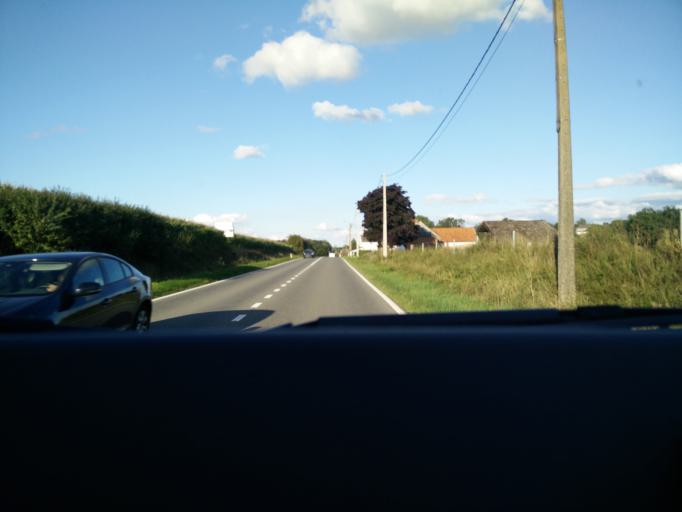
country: BE
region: Wallonia
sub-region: Province de Namur
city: Florennes
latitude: 50.2310
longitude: 4.6764
